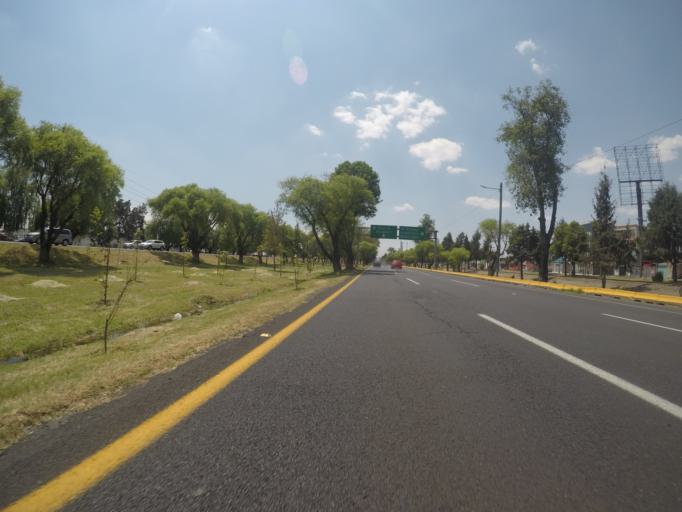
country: MX
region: Mexico
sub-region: San Mateo Atenco
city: Santa Maria la Asuncion
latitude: 19.2866
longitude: -99.5642
